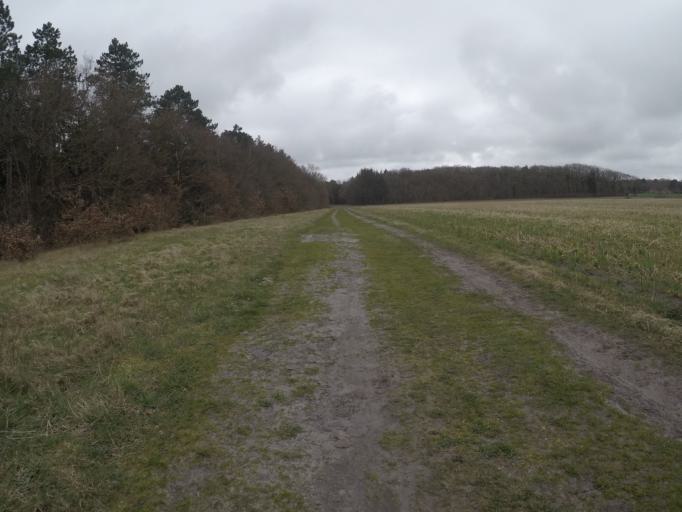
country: DE
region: Lower Saxony
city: Nordholz
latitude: 53.8212
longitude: 8.5988
